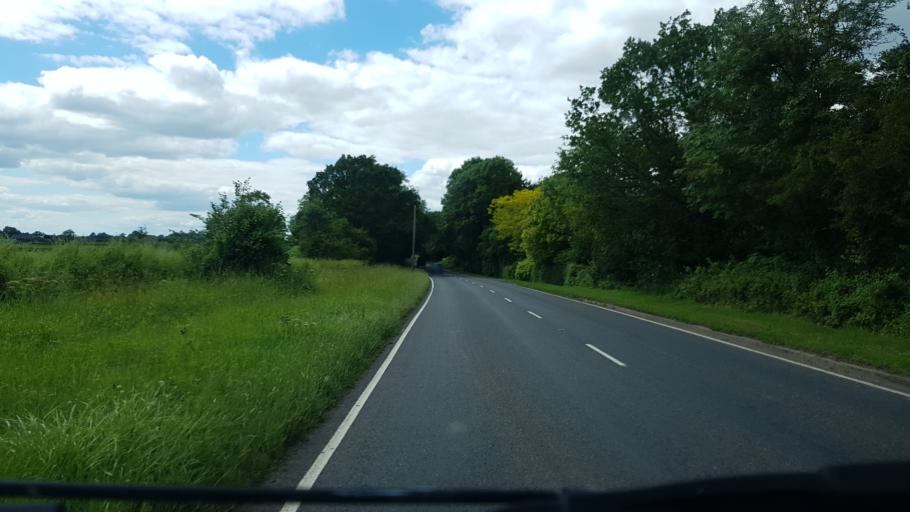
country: GB
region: England
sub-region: Worcestershire
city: Droitwich
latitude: 52.2626
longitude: -2.0964
